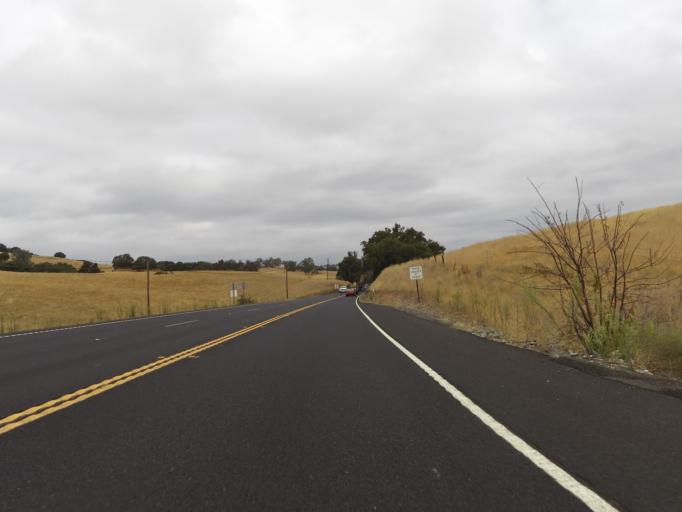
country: US
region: California
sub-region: Calaveras County
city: San Andreas
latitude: 38.1474
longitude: -120.6400
